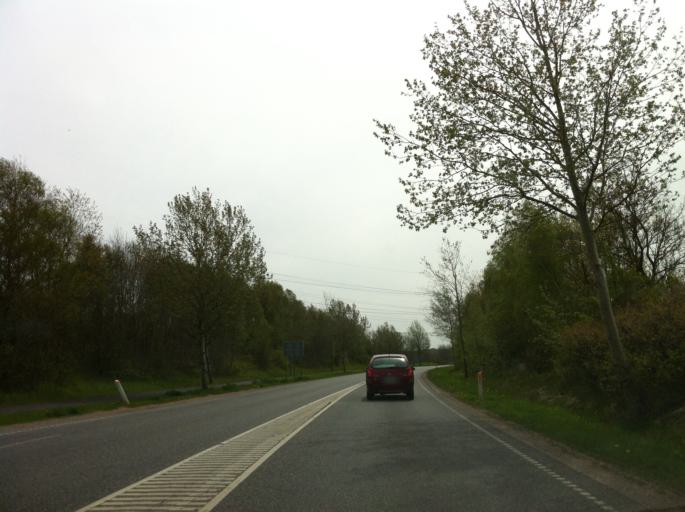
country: DK
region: Capital Region
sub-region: Frederikssund Kommune
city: Slangerup
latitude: 55.8465
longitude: 12.1518
